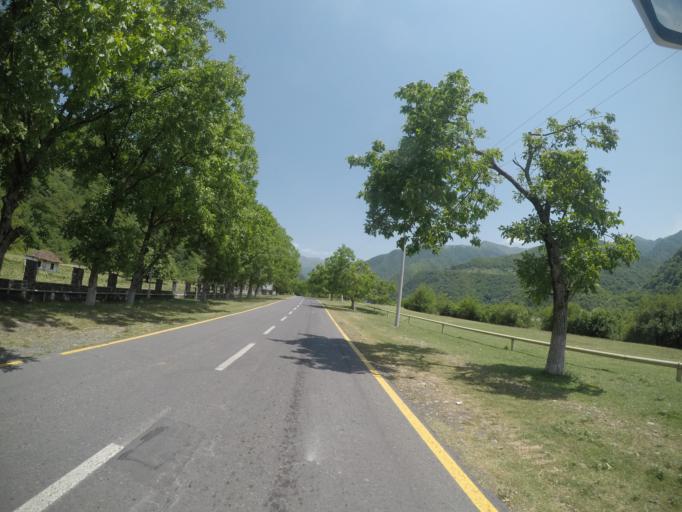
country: AZ
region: Qakh Rayon
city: Qaxbas
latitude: 41.4476
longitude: 46.9987
